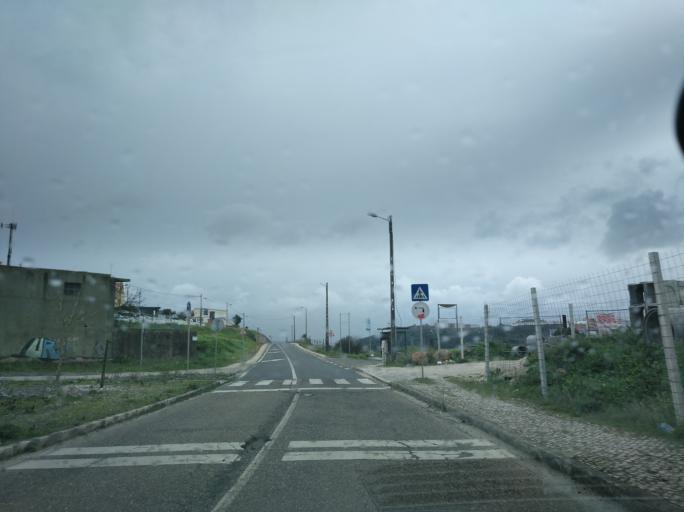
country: PT
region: Lisbon
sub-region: Odivelas
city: Canecas
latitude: 38.7954
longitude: -9.2298
